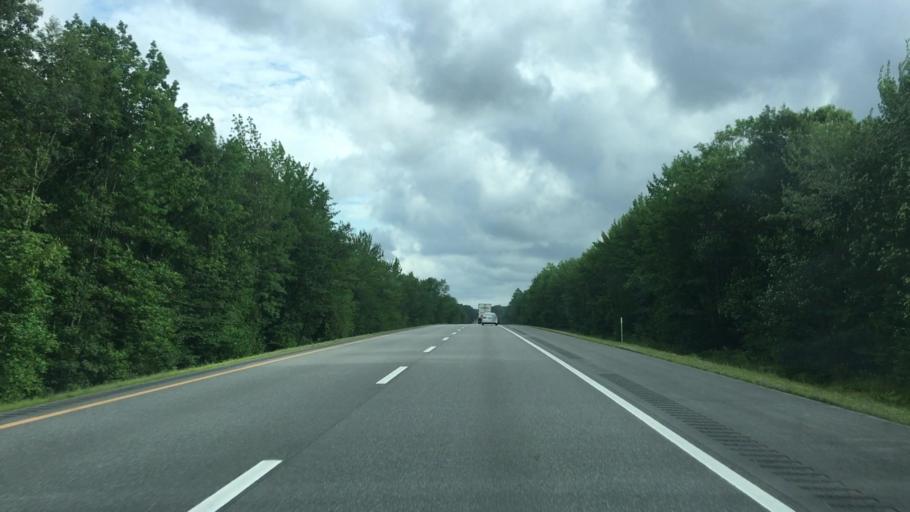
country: US
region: Maine
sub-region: Somerset County
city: Pittsfield
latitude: 44.7639
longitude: -69.4144
